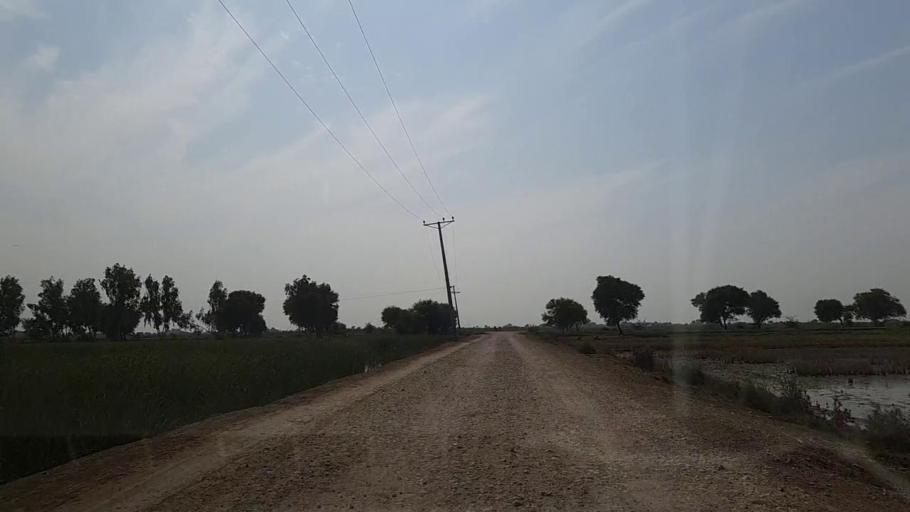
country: PK
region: Sindh
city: Mirpur Batoro
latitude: 24.6123
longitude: 68.2364
